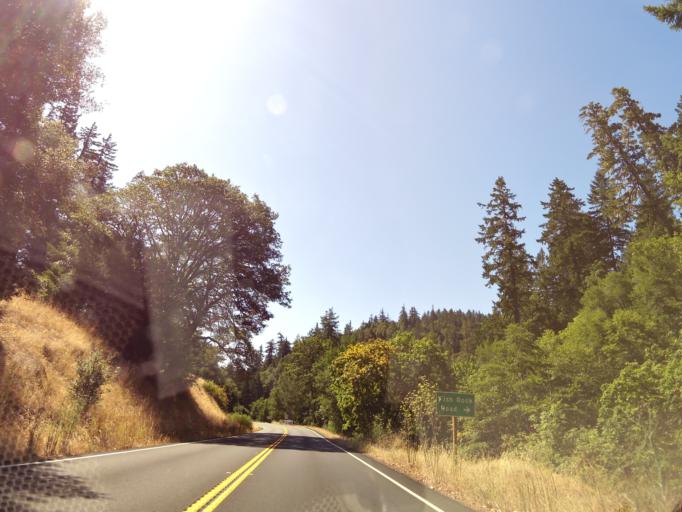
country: US
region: California
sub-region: Mendocino County
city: Boonville
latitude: 38.9222
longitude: -123.2943
